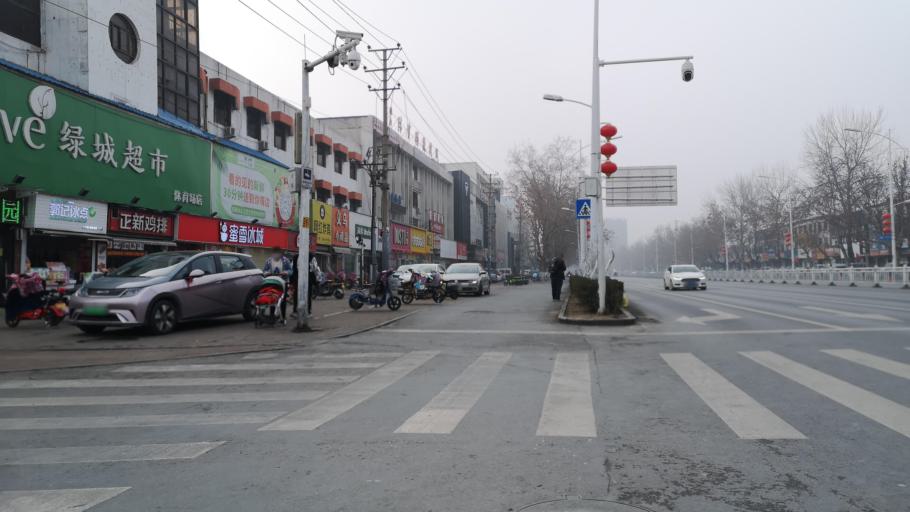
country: CN
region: Henan Sheng
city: Zhongyuanlu
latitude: 35.7776
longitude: 115.0423
